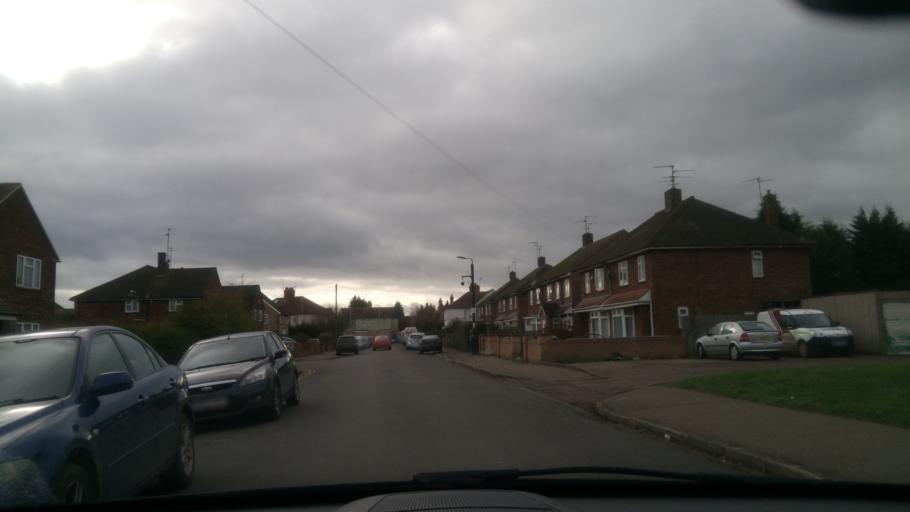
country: GB
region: England
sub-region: Peterborough
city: Peterborough
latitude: 52.5796
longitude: -0.2260
